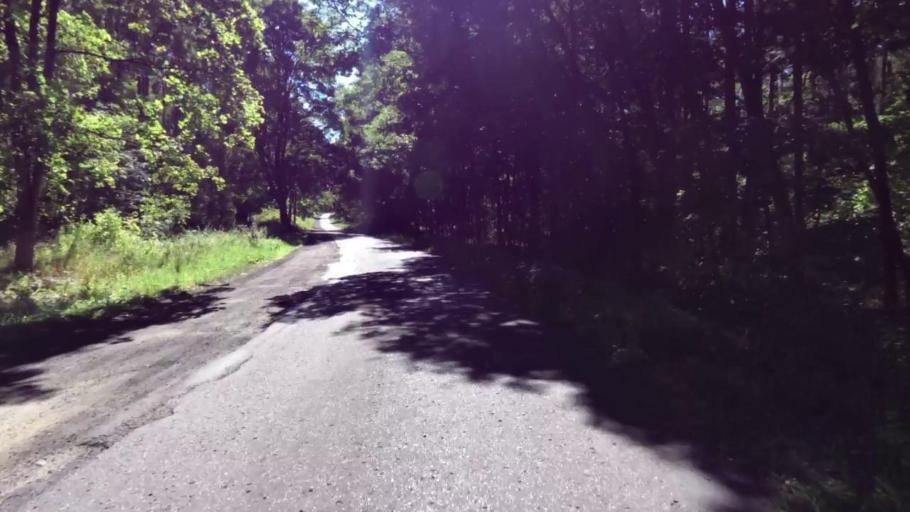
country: PL
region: West Pomeranian Voivodeship
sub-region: Powiat szczecinecki
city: Szczecinek
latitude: 53.7077
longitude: 16.6256
